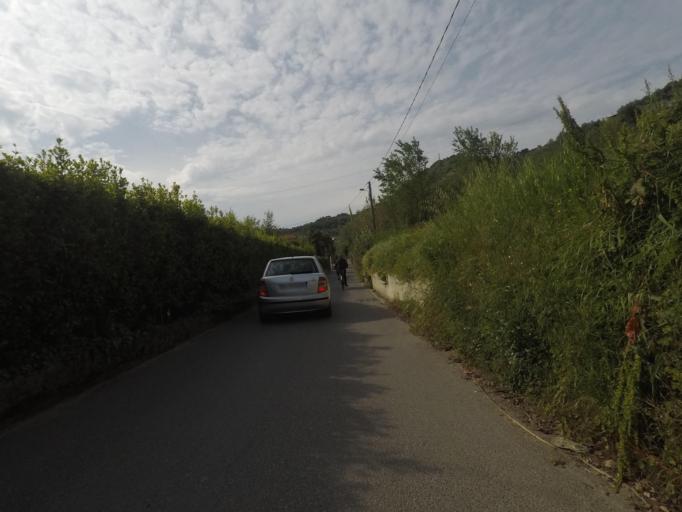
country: IT
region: Tuscany
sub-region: Provincia di Massa-Carrara
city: Massa
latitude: 44.0442
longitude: 10.1053
